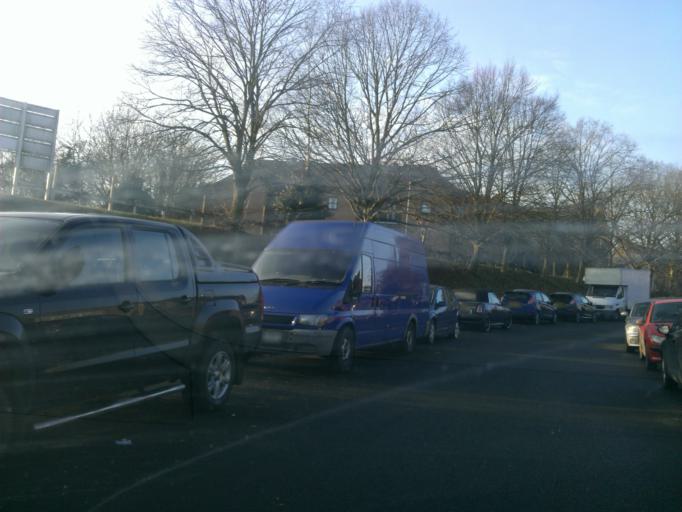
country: GB
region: England
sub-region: Essex
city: Great Dunmow
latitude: 51.8682
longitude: 0.3673
